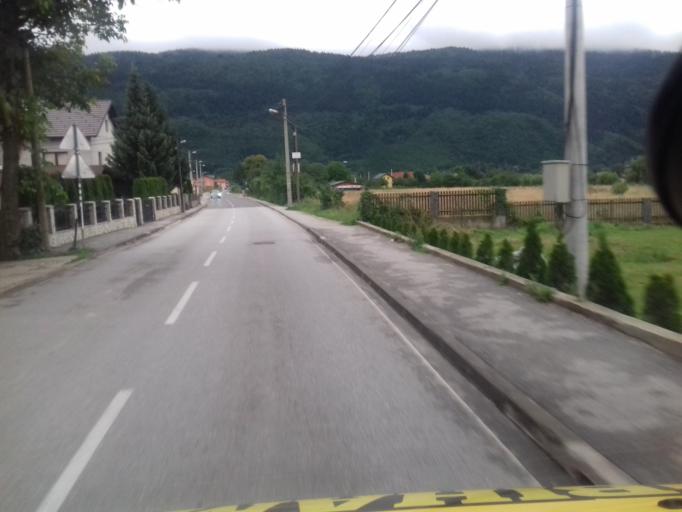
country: BA
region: Federation of Bosnia and Herzegovina
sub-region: Kanton Sarajevo
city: Sarajevo
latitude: 43.8144
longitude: 18.3068
